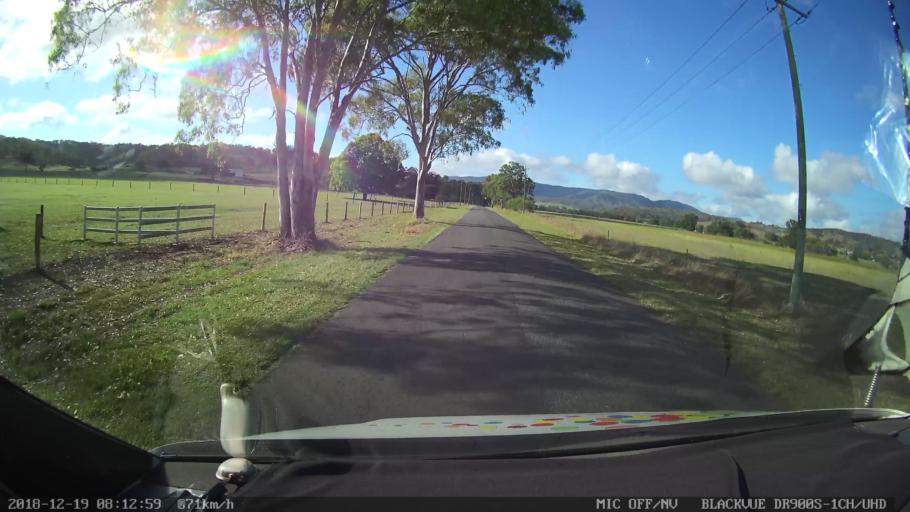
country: AU
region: Queensland
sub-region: Logan
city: Cedar Vale
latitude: -28.2337
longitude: 152.8914
